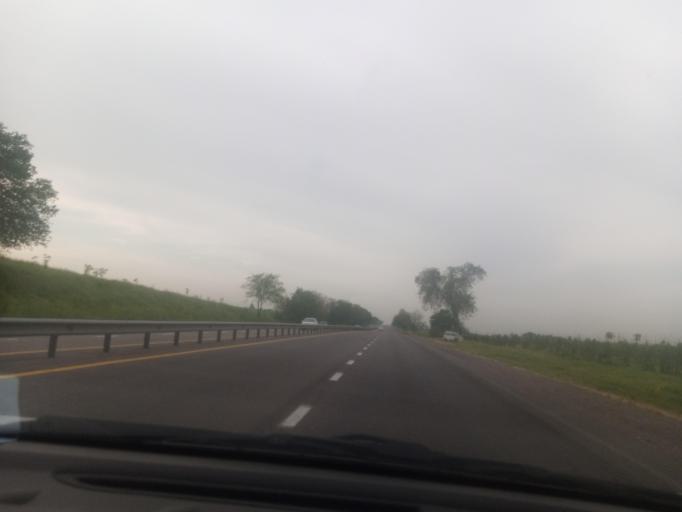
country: UZ
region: Toshkent
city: Tuytepa
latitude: 41.1074
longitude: 69.4512
